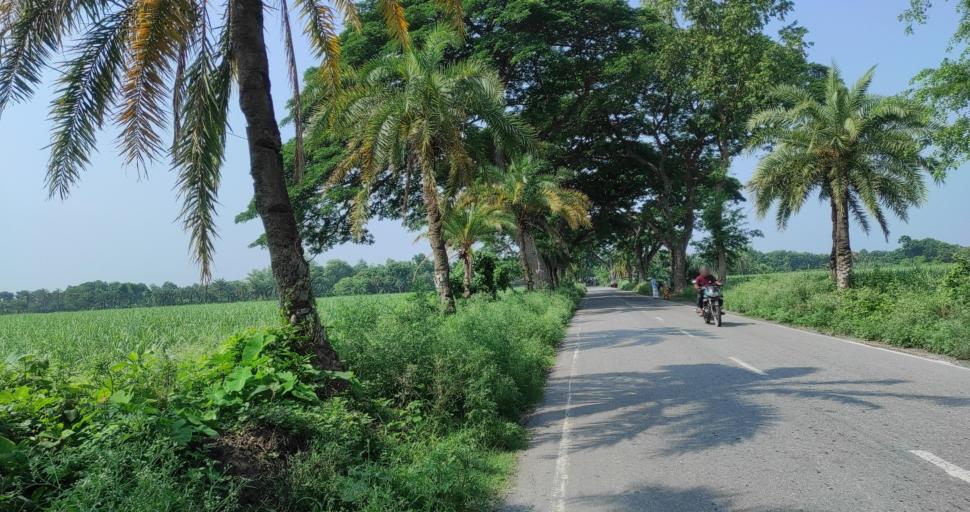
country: BD
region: Rajshahi
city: Ishurdi
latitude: 24.2640
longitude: 89.0503
